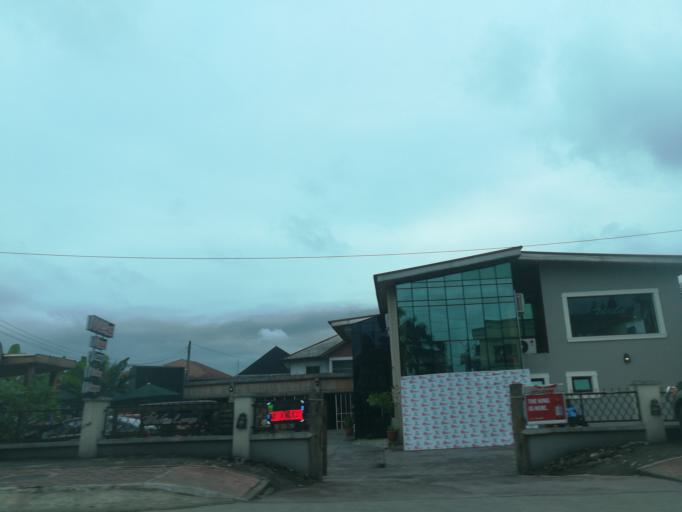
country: NG
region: Rivers
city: Port Harcourt
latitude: 4.8206
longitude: 6.9964
